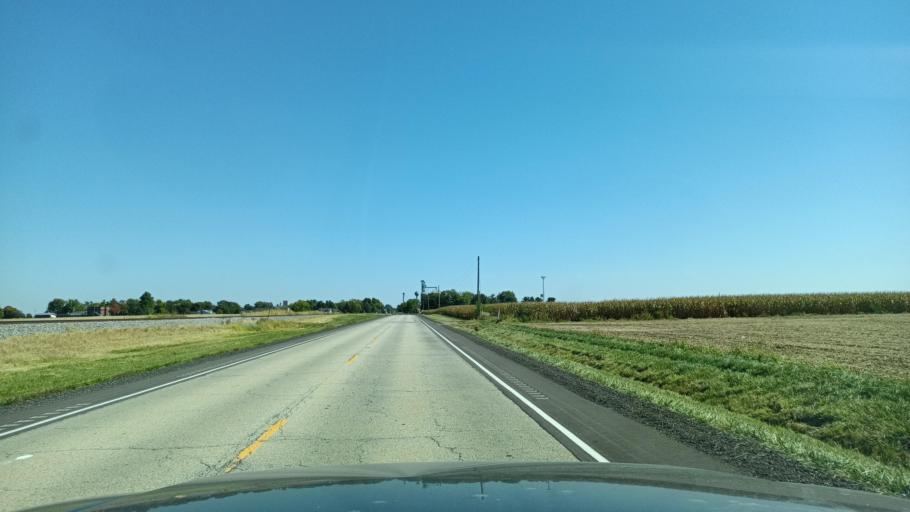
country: US
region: Illinois
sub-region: Woodford County
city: Eureka
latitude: 40.6274
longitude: -89.2904
